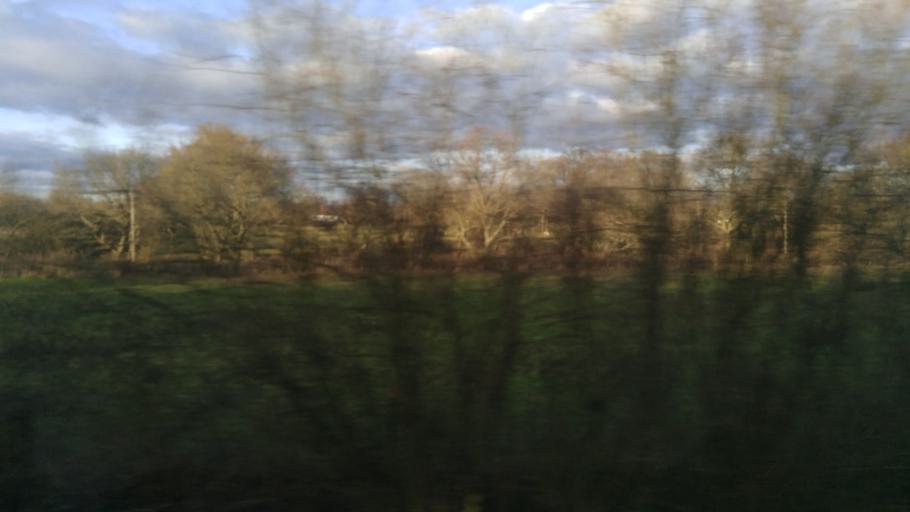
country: GB
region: England
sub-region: Kent
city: Headcorn
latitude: 51.1638
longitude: 0.6521
